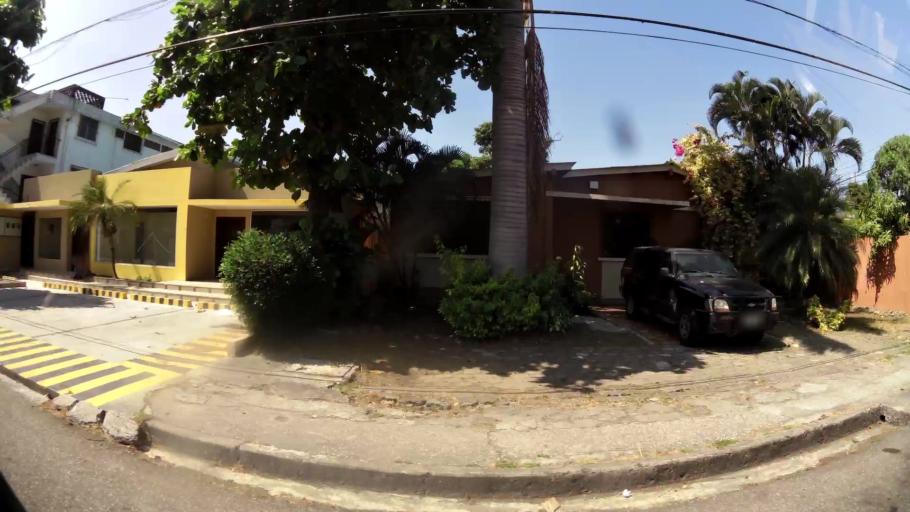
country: EC
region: Guayas
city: Guayaquil
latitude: -2.1674
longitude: -79.9127
